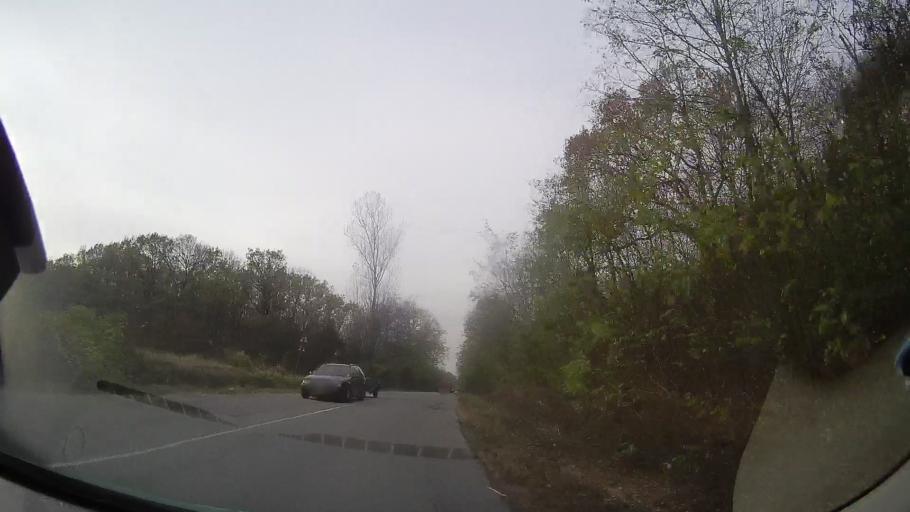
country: RO
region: Prahova
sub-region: Comuna Balta Doamnei
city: Balta Doamnei
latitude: 44.7599
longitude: 26.1356
